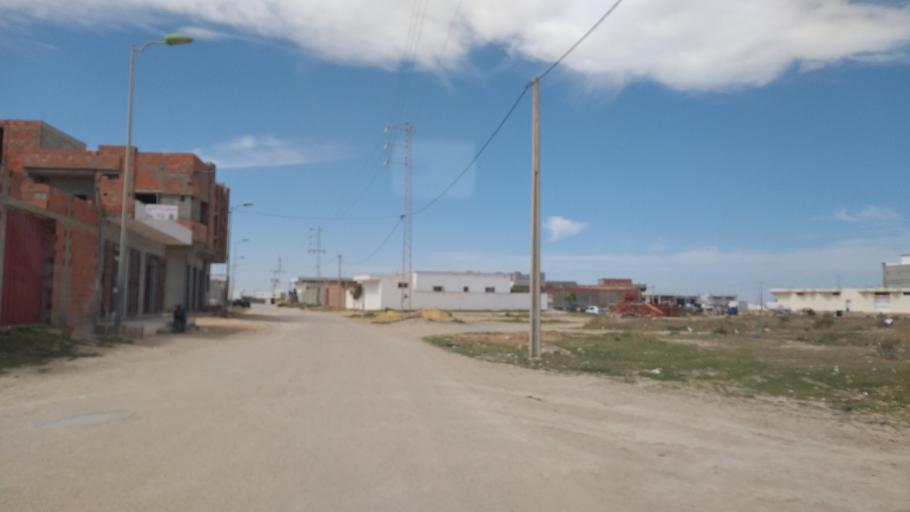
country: TN
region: Al Mahdiyah
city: El Jem
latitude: 35.3048
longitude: 10.6936
